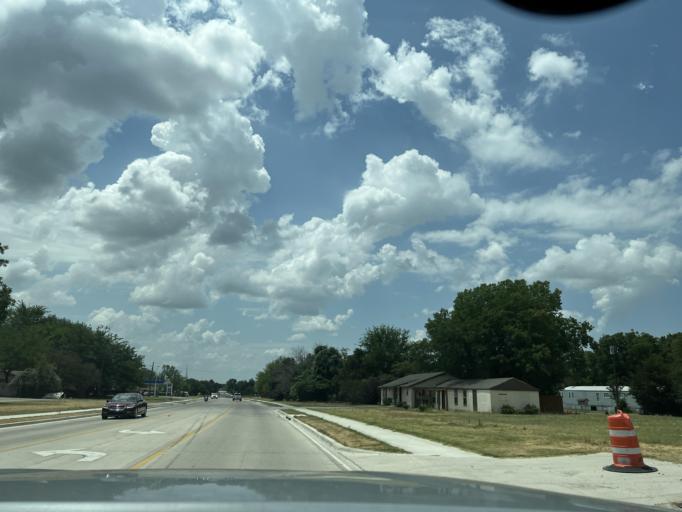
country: US
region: Texas
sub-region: Parker County
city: Springtown
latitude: 32.9755
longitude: -97.6858
